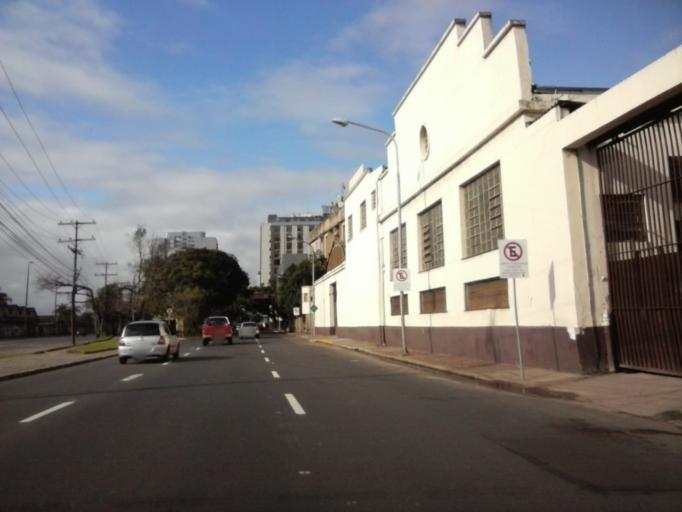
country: BR
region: Rio Grande do Sul
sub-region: Porto Alegre
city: Porto Alegre
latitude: -30.0308
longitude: -51.2378
